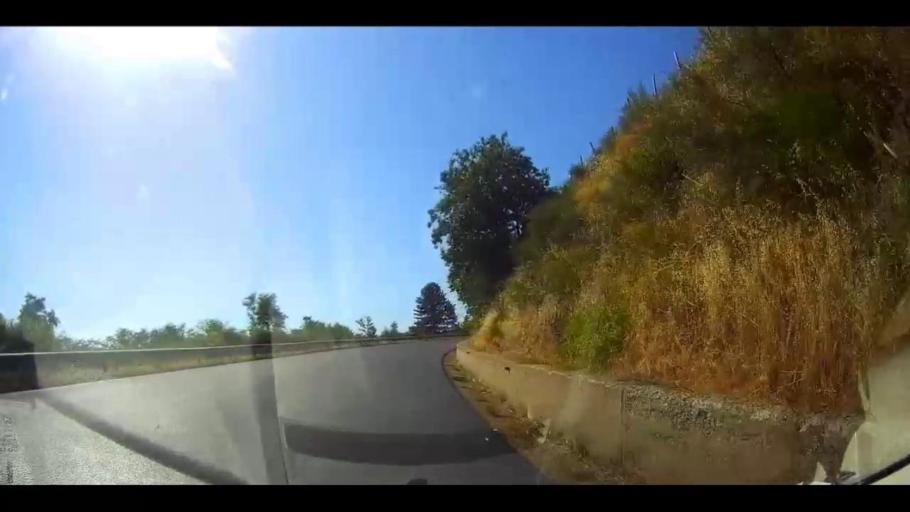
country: IT
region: Calabria
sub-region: Provincia di Cosenza
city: Celico
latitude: 39.3205
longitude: 16.3698
